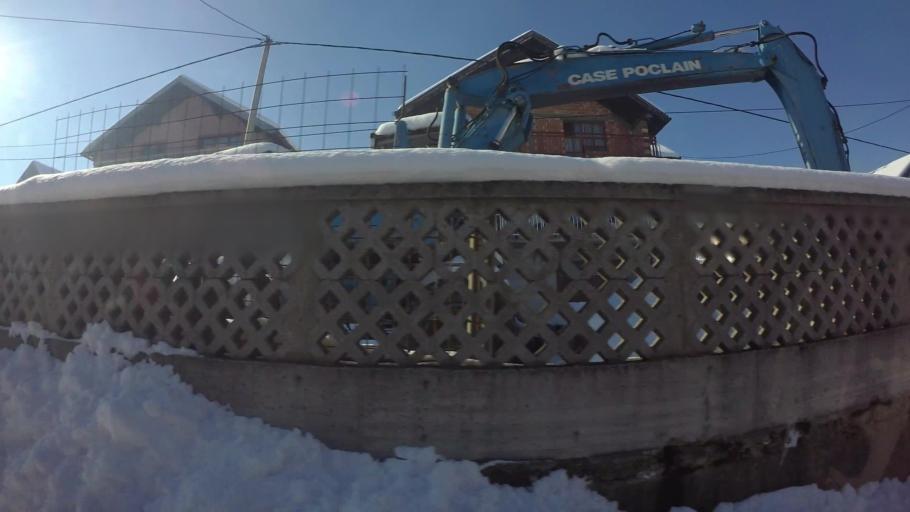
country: BA
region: Federation of Bosnia and Herzegovina
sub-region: Kanton Sarajevo
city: Sarajevo
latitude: 43.8186
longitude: 18.3739
